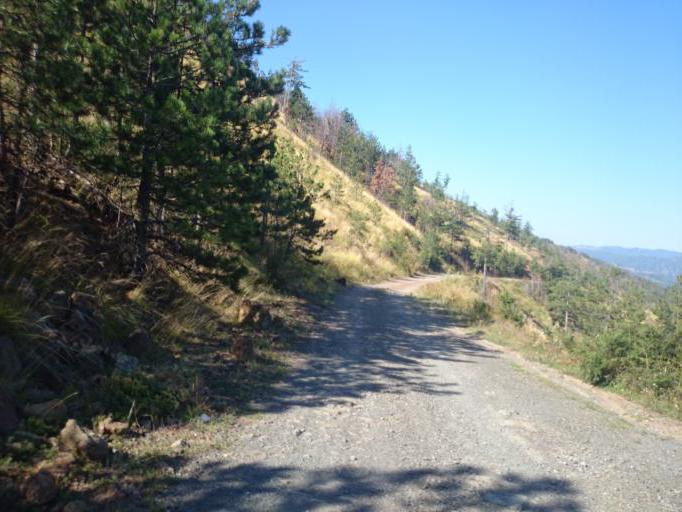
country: AL
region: Diber
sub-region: Rrethi i Bulqizes
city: Martanesh
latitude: 41.4034
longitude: 20.2847
